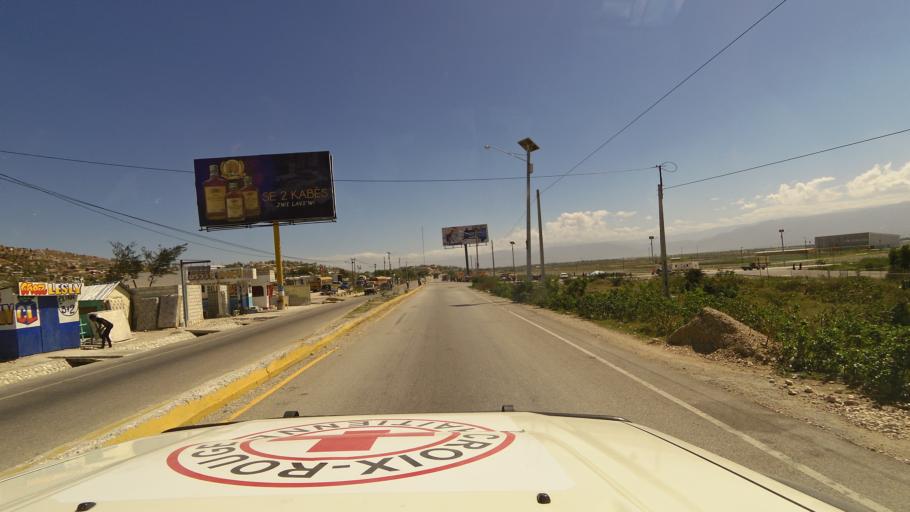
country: HT
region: Ouest
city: Croix des Bouquets
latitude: 18.6604
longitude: -72.2919
